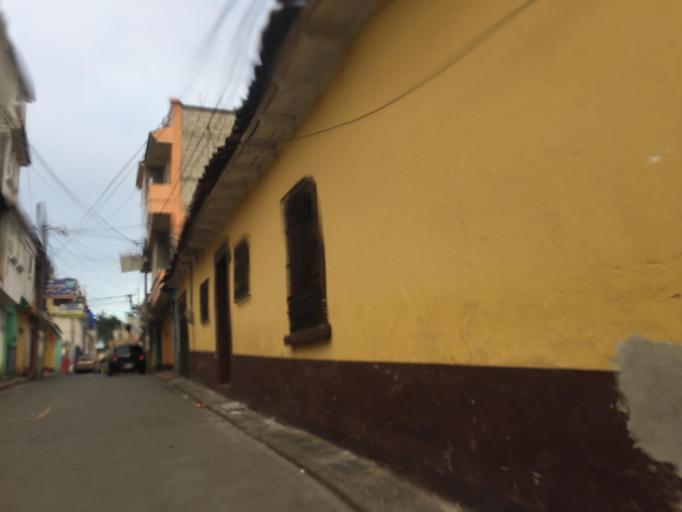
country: GT
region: Totonicapan
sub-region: Municipio de Totonicapan
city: Totonicapan
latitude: 14.9097
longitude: -91.3616
